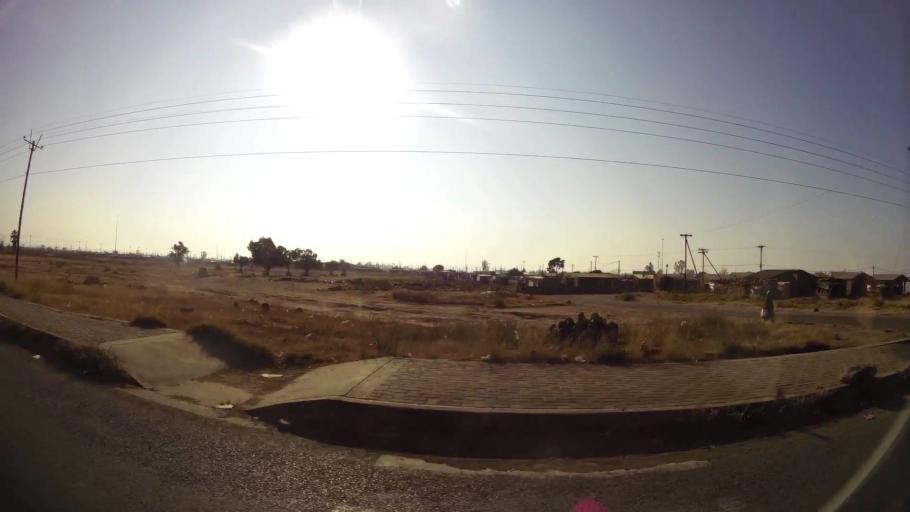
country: ZA
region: Orange Free State
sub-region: Mangaung Metropolitan Municipality
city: Bloemfontein
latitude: -29.1759
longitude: 26.2642
